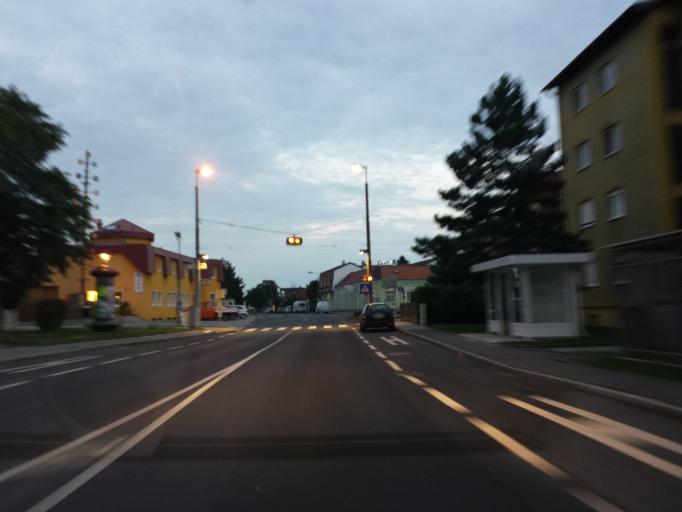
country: AT
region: Lower Austria
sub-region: Politischer Bezirk Baden
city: Oberwaltersdorf
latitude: 47.9755
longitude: 16.3227
